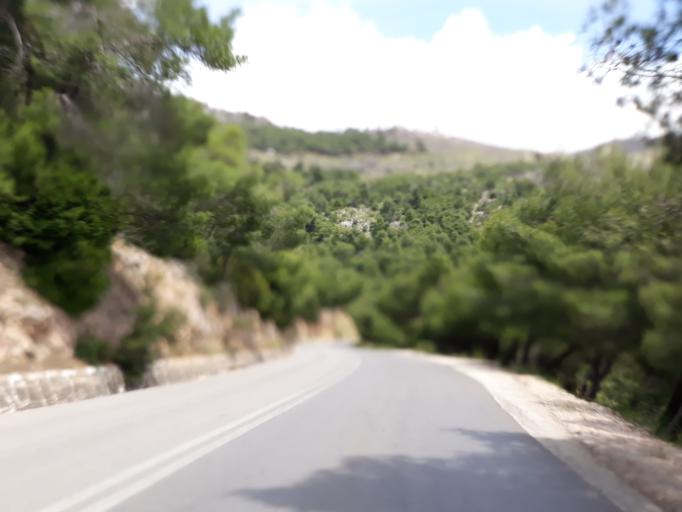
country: GR
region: Attica
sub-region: Nomarchia Dytikis Attikis
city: Magoula
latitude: 38.1485
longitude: 23.5197
